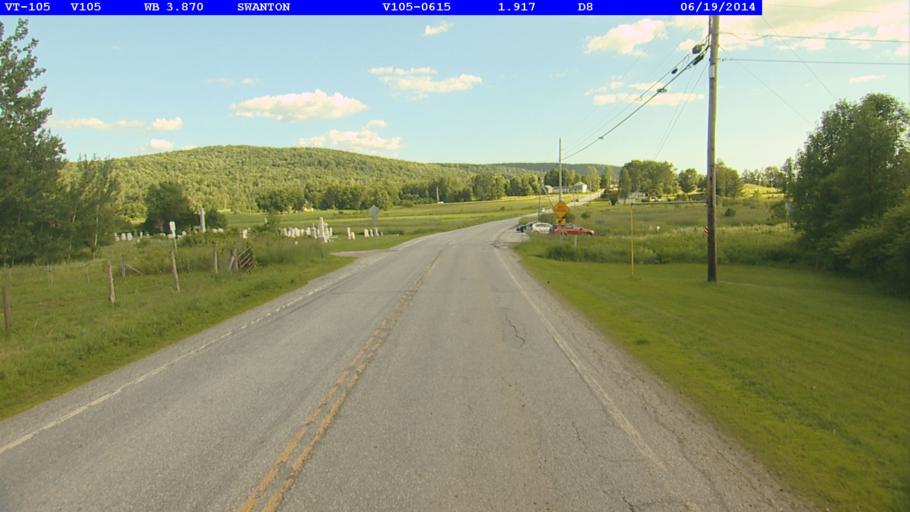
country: US
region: Vermont
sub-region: Franklin County
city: Saint Albans
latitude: 44.8600
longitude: -73.0325
